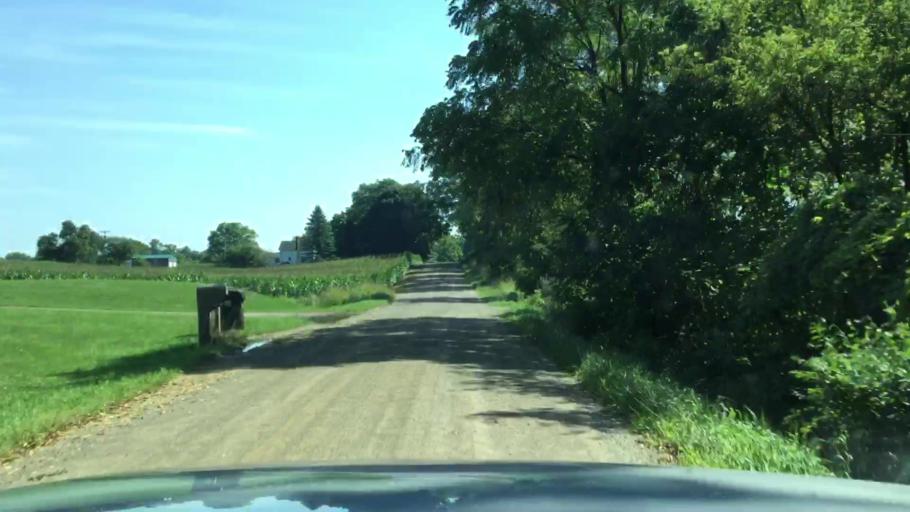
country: US
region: Michigan
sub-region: Lenawee County
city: Manitou Beach-Devils Lake
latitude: 41.9936
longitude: -84.3372
